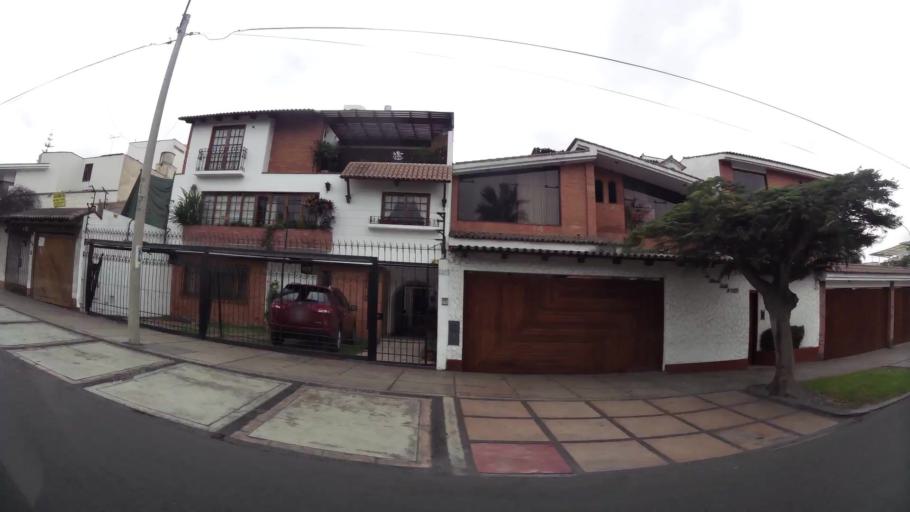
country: PE
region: Lima
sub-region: Lima
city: Surco
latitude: -12.1202
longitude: -76.9845
